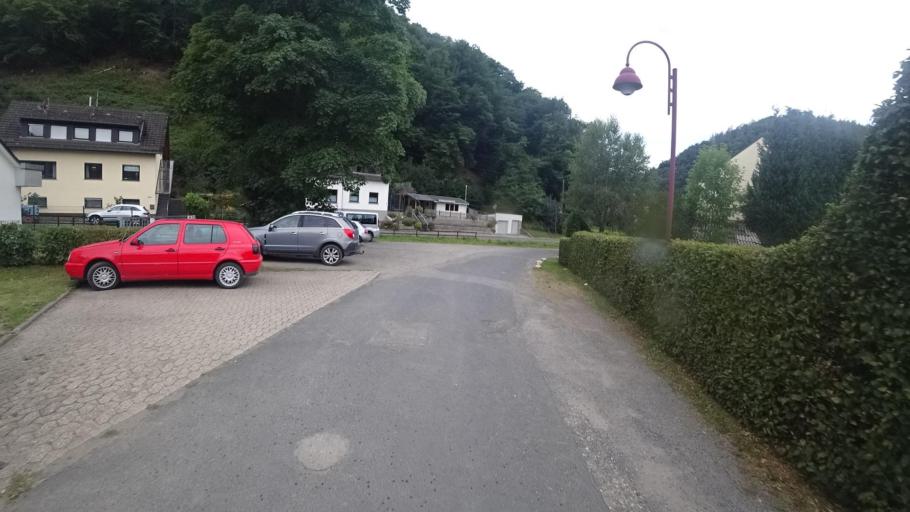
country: DE
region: Rheinland-Pfalz
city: Ahrbruck
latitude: 50.4823
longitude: 6.9850
